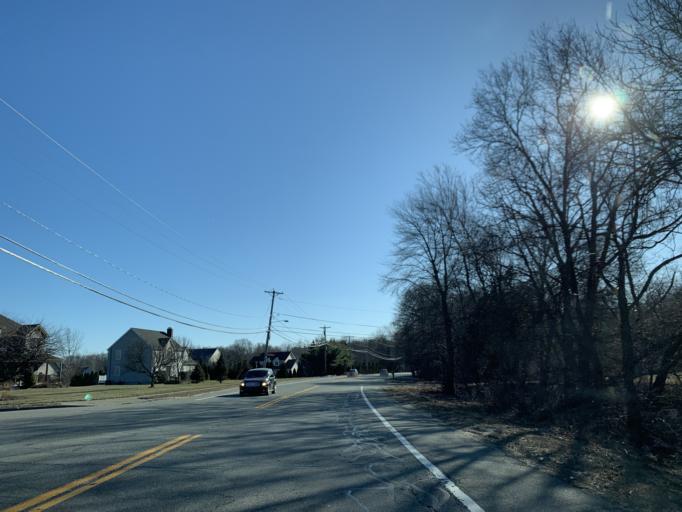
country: US
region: Rhode Island
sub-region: Providence County
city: North Providence
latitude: 41.8849
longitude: -71.4600
